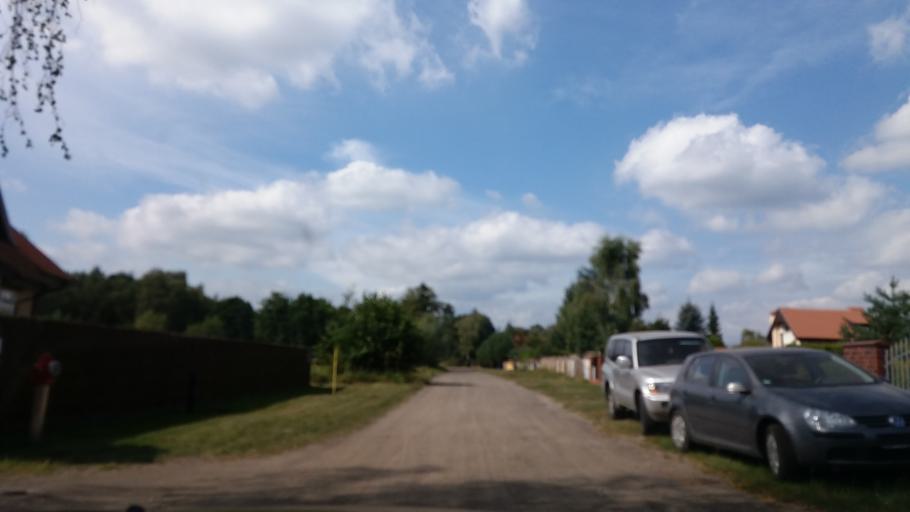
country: PL
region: West Pomeranian Voivodeship
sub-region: Powiat stargardzki
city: Kobylanka
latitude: 53.3557
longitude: 14.9236
